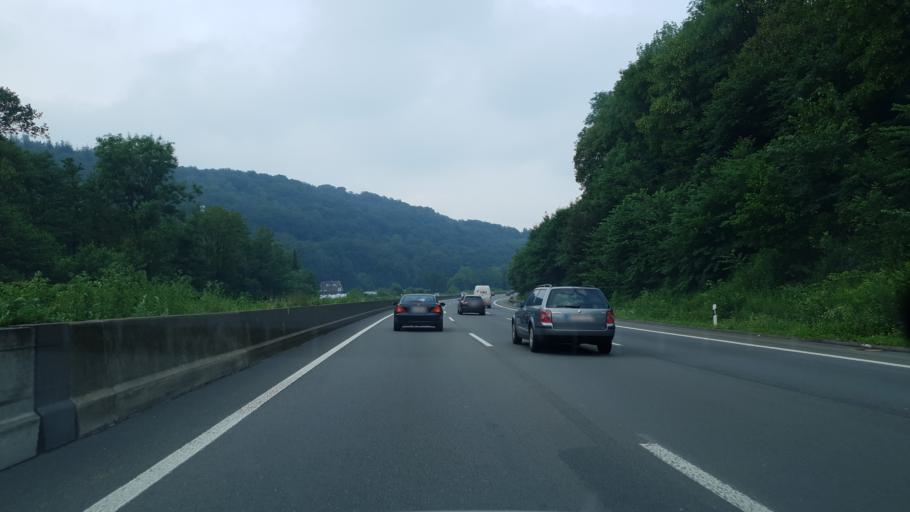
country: DE
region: North Rhine-Westphalia
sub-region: Regierungsbezirk Dusseldorf
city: Wuppertal
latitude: 51.2478
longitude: 7.2256
